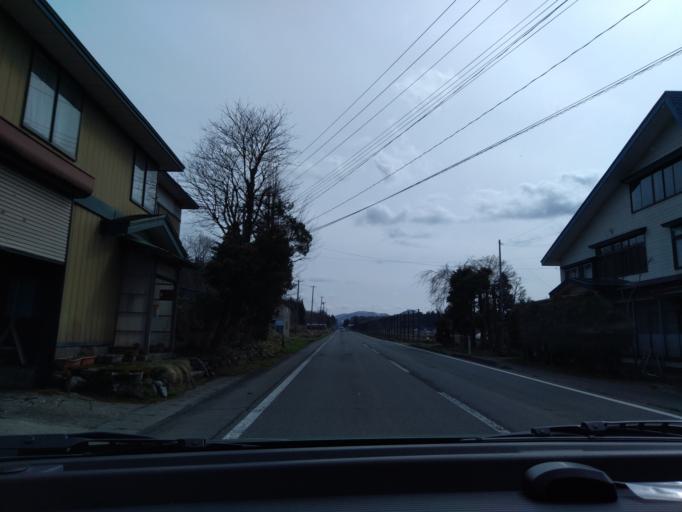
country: JP
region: Akita
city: Yokotemachi
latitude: 39.2941
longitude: 140.7322
